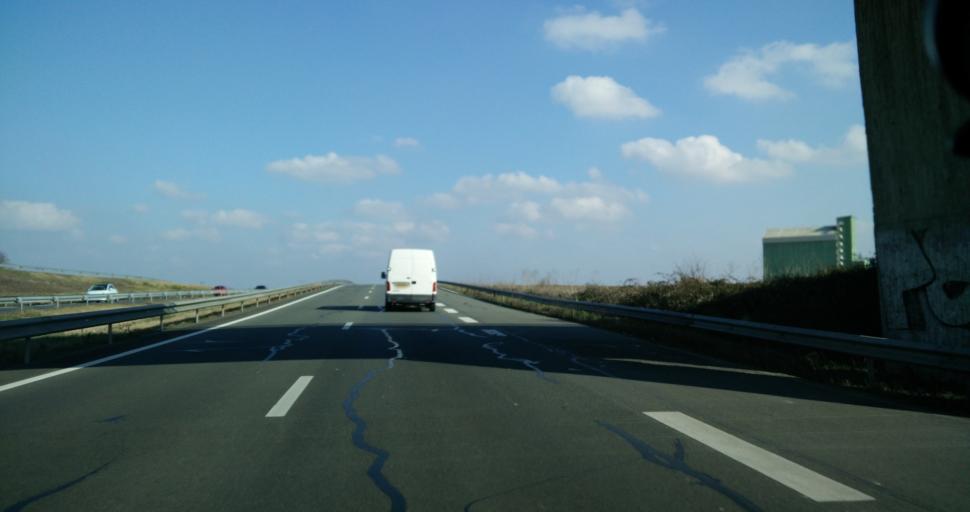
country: FR
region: Poitou-Charentes
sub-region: Departement de la Charente-Maritime
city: Verines
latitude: 46.2143
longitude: -0.9894
